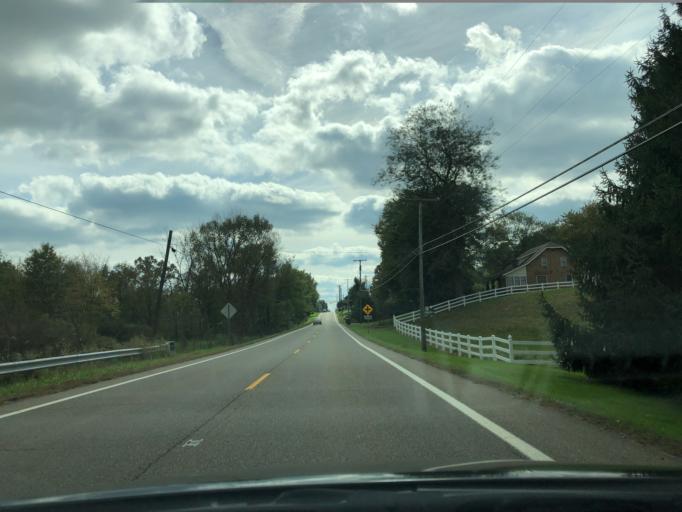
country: US
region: Ohio
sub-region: Stark County
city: Brewster
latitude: 40.7313
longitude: -81.5965
